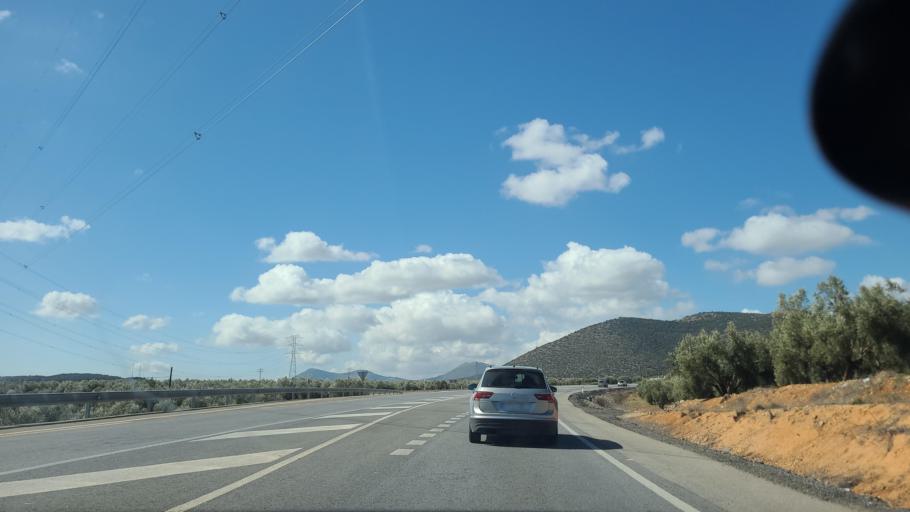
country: ES
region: Andalusia
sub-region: Provincia de Granada
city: Iznalloz
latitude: 37.3994
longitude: -3.5495
